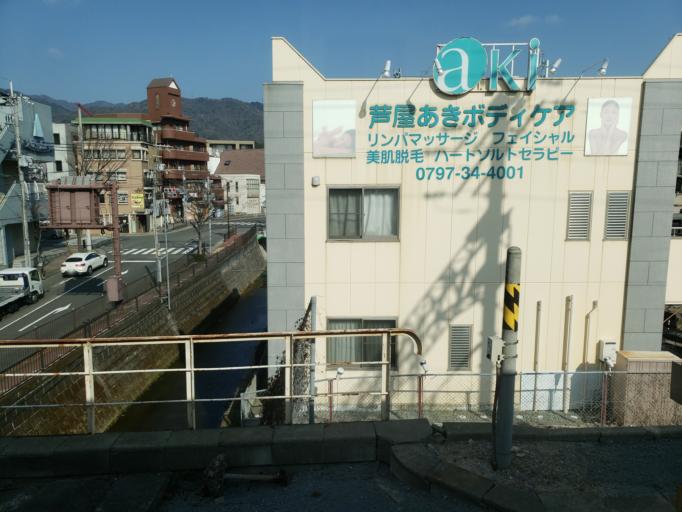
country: JP
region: Hyogo
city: Ashiya
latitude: 34.7352
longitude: 135.3105
